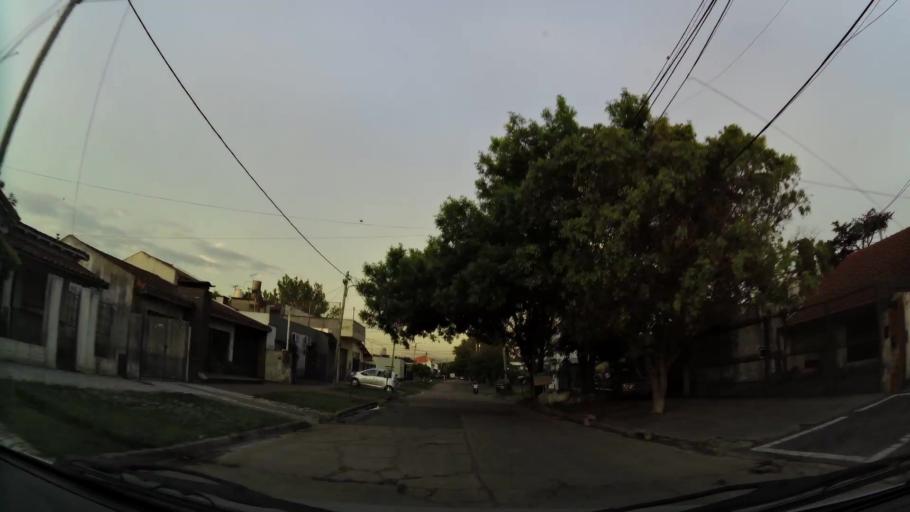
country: AR
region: Buenos Aires
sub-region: Partido de Lomas de Zamora
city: Lomas de Zamora
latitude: -34.7678
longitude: -58.3780
